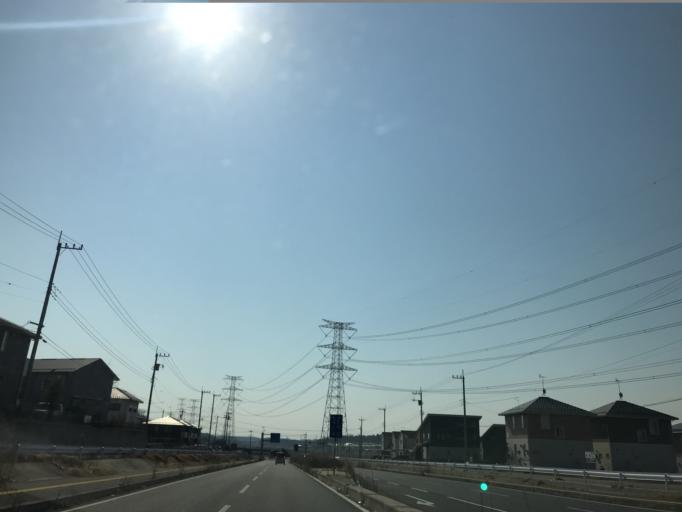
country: JP
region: Ibaraki
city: Mitsukaido
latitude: 36.0350
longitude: 140.0633
